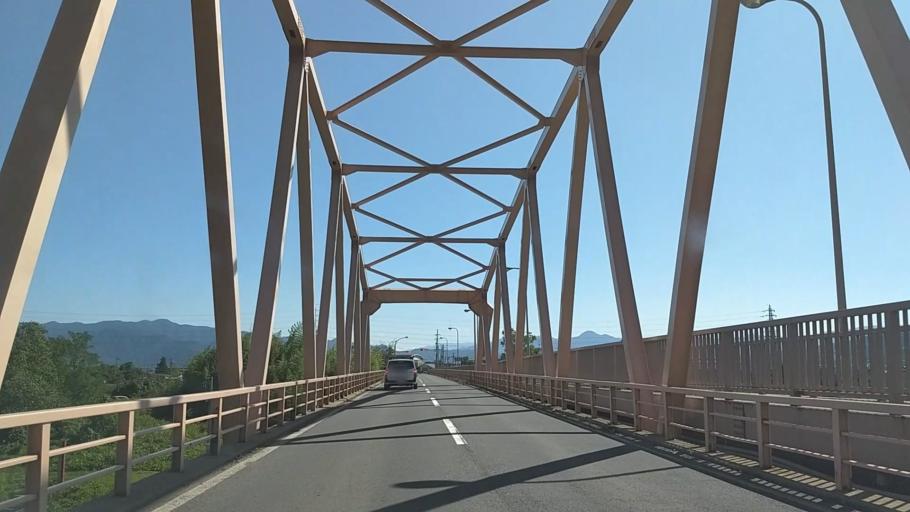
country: JP
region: Nagano
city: Nagano-shi
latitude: 36.6210
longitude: 138.1415
